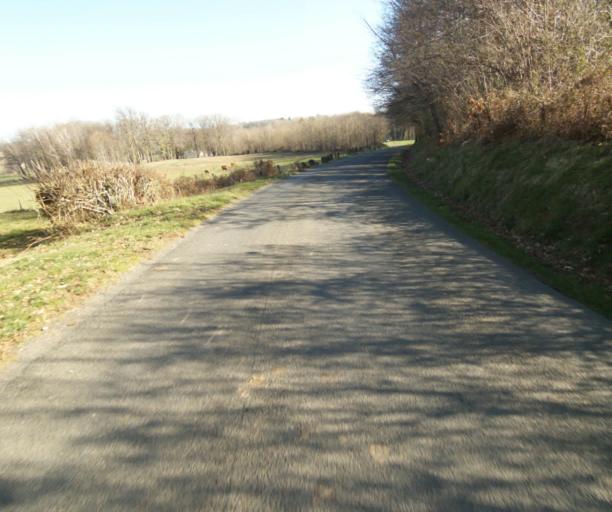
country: FR
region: Limousin
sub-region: Departement de la Correze
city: Saint-Clement
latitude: 45.3768
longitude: 1.6441
